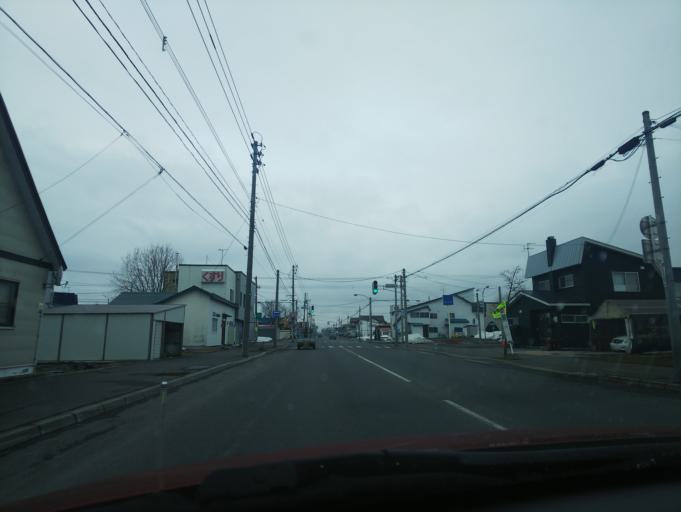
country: JP
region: Hokkaido
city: Nayoro
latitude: 44.3546
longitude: 142.4503
